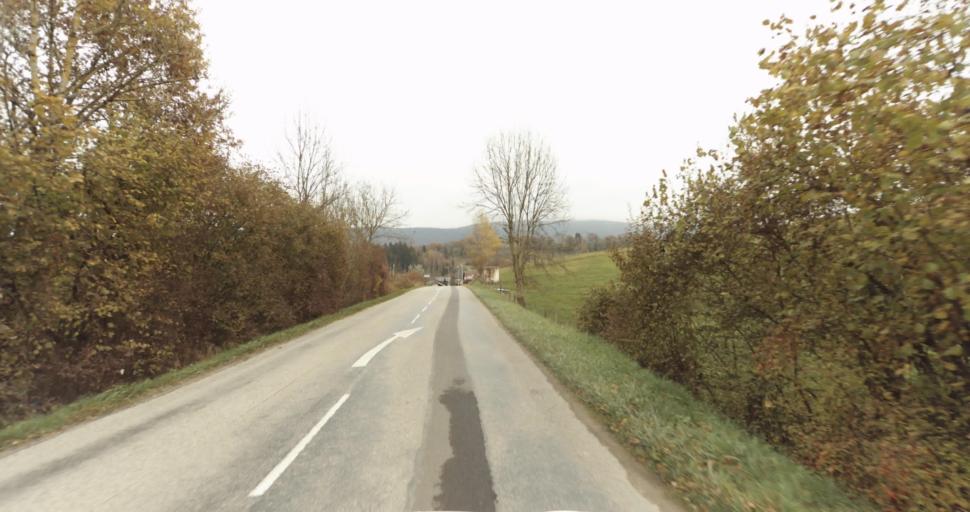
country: FR
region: Rhone-Alpes
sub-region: Departement de la Haute-Savoie
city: Seynod
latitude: 45.8645
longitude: 6.0664
